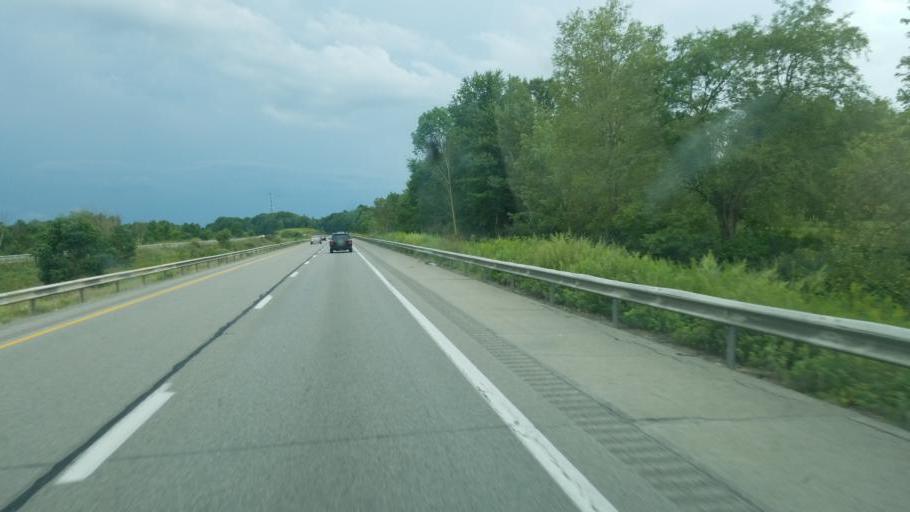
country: US
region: Pennsylvania
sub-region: Mercer County
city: Mercer
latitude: 41.2280
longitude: -80.1630
